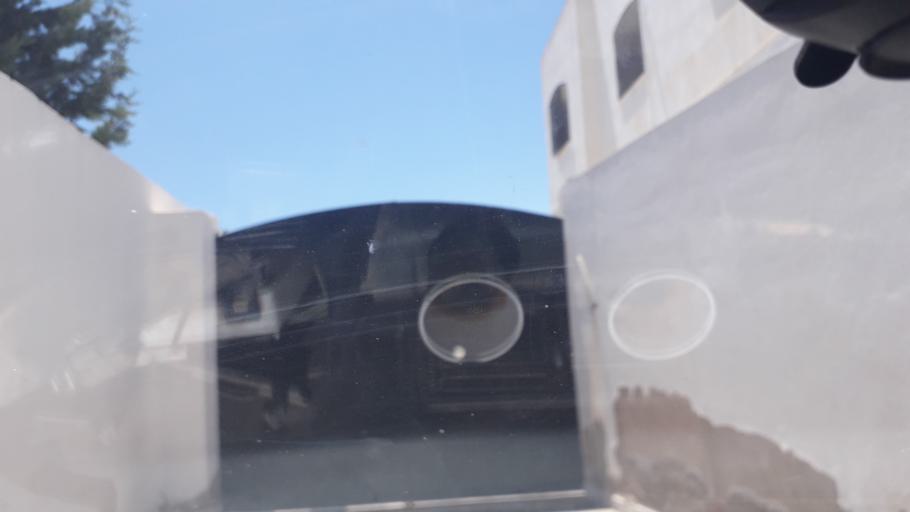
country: TN
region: Safaqis
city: Al Qarmadah
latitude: 34.8146
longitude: 10.7642
